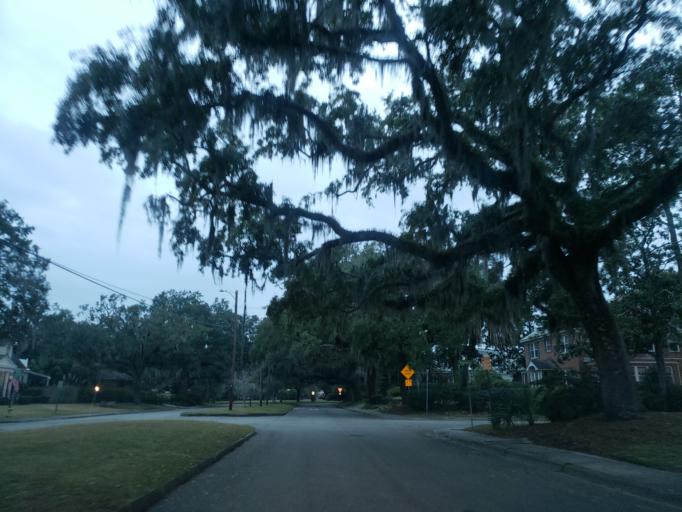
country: US
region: Georgia
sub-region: Chatham County
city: Thunderbolt
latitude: 32.0561
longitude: -81.0657
